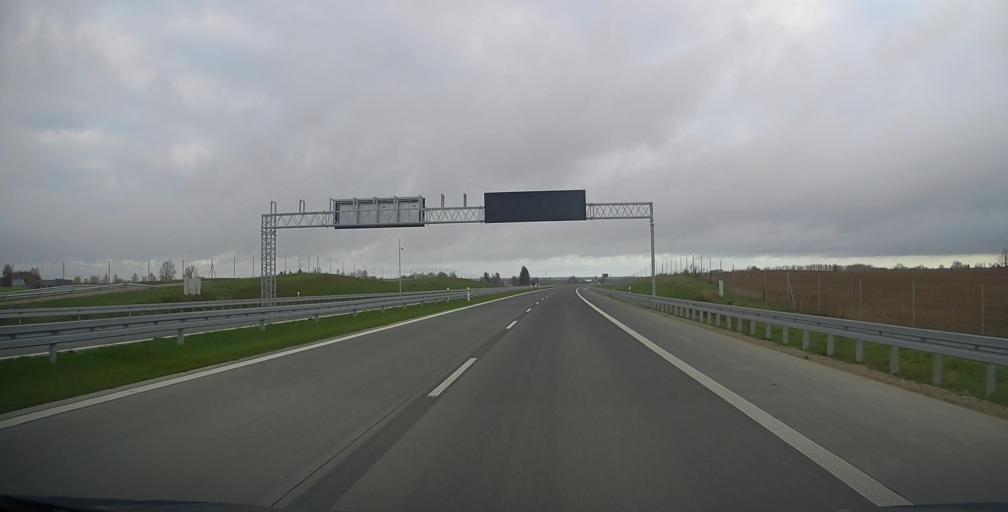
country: PL
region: Podlasie
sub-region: Powiat suwalski
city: Raczki
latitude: 53.9572
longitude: 22.7714
